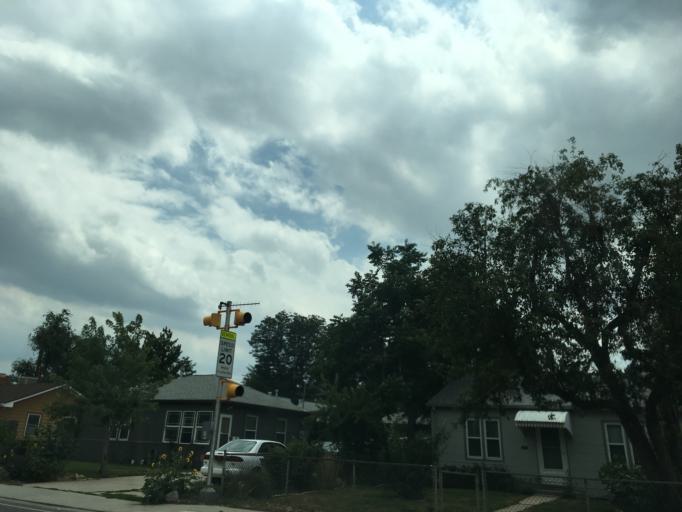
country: US
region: Colorado
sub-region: Arapahoe County
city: Sheridan
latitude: 39.6822
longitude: -105.0311
